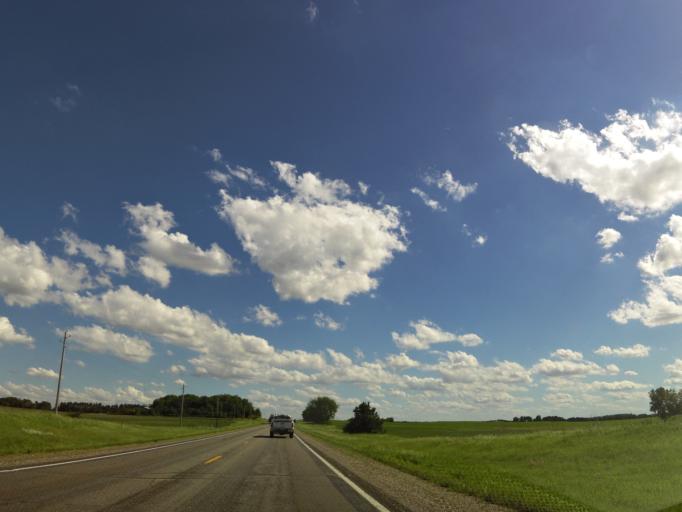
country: US
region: Minnesota
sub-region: Meeker County
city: Dassel
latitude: 45.1772
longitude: -94.3175
